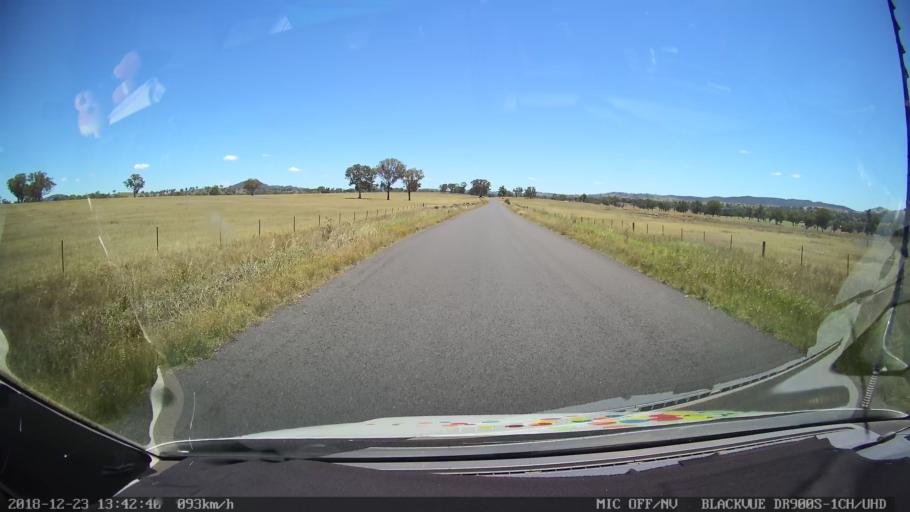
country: AU
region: New South Wales
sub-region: Armidale Dumaresq
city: Armidale
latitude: -30.4794
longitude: 151.1602
